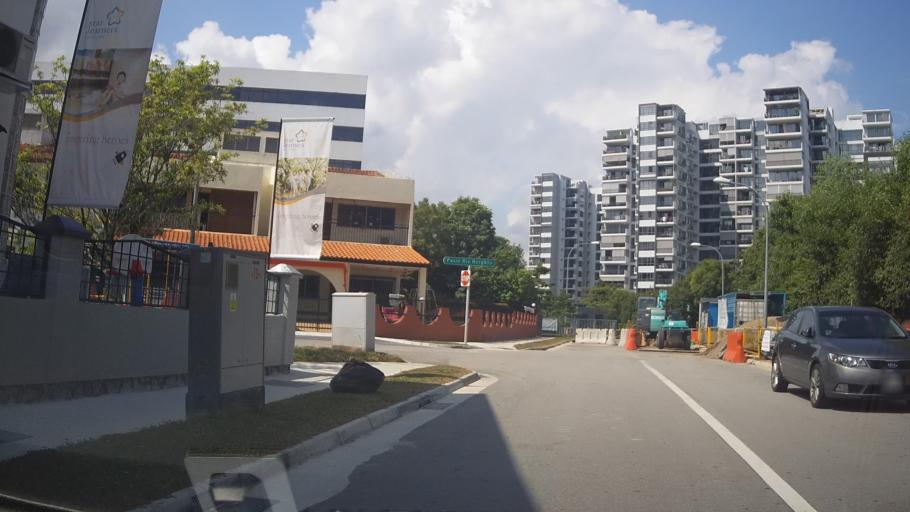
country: MY
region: Johor
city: Kampung Pasir Gudang Baru
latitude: 1.3827
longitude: 103.9425
